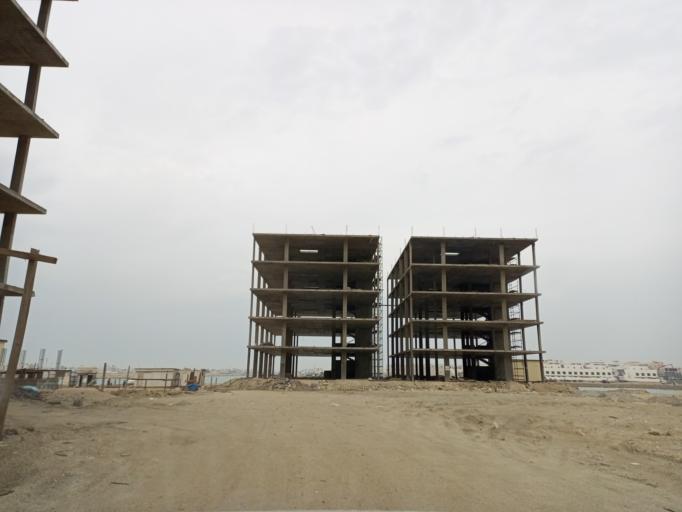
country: BH
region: Muharraq
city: Al Hadd
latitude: 26.2305
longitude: 50.6423
